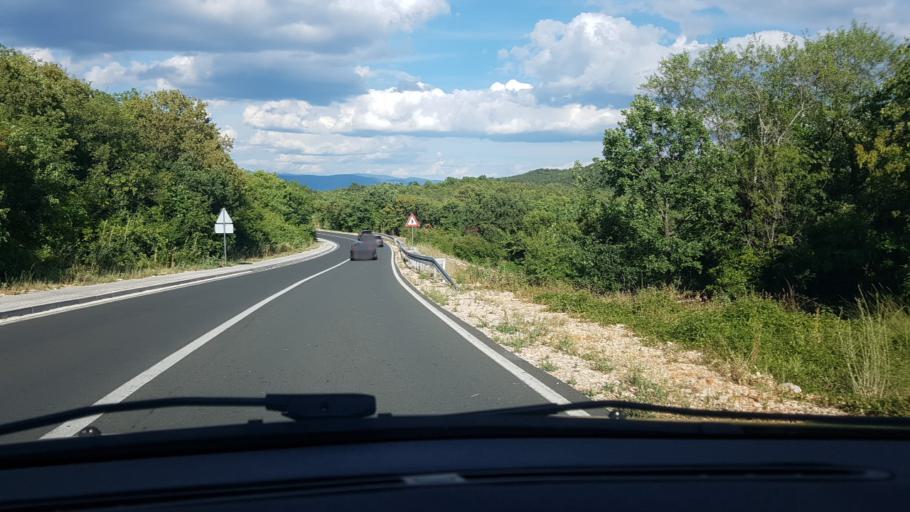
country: HR
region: Splitsko-Dalmatinska
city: Grubine
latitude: 43.4222
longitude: 17.1182
